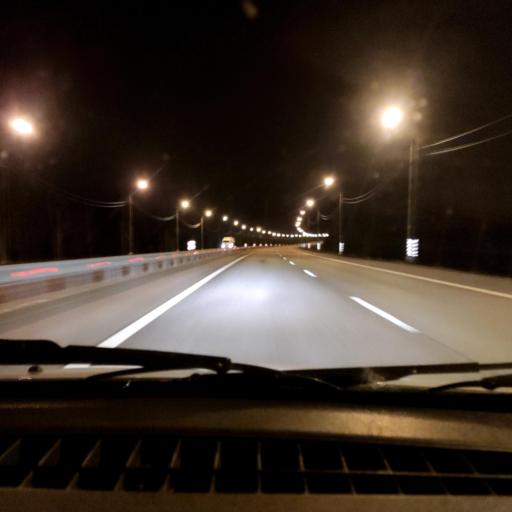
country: RU
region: Lipetsk
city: Zadonsk
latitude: 52.3780
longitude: 38.8853
